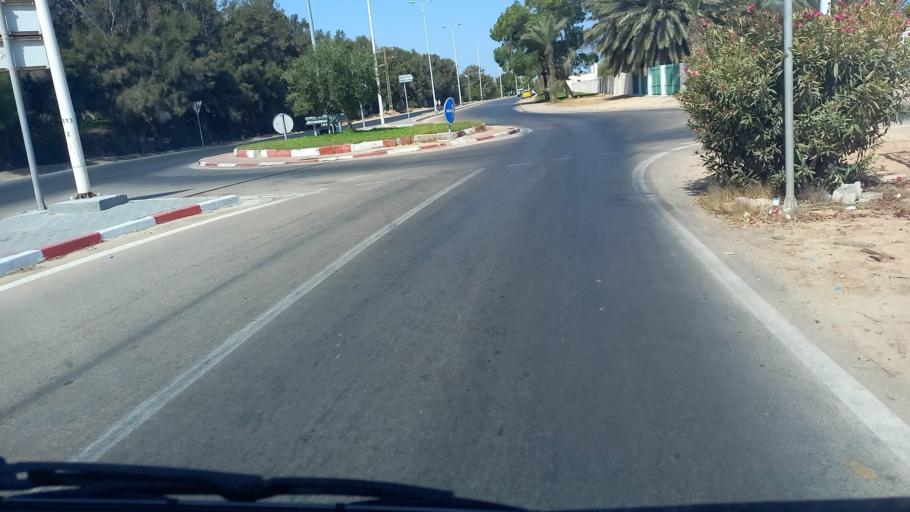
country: TN
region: Madanin
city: Midoun
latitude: 33.8263
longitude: 11.0163
